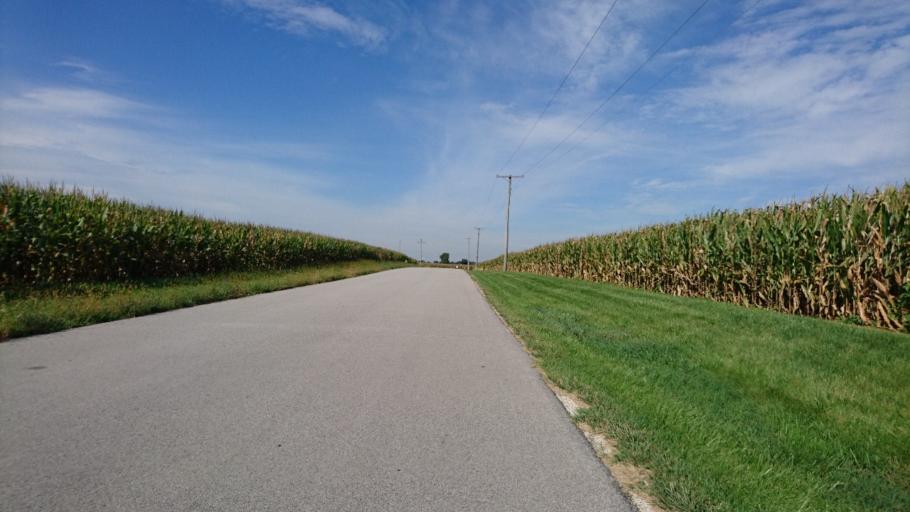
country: US
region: Illinois
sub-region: Will County
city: Elwood
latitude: 41.4156
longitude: -88.0755
